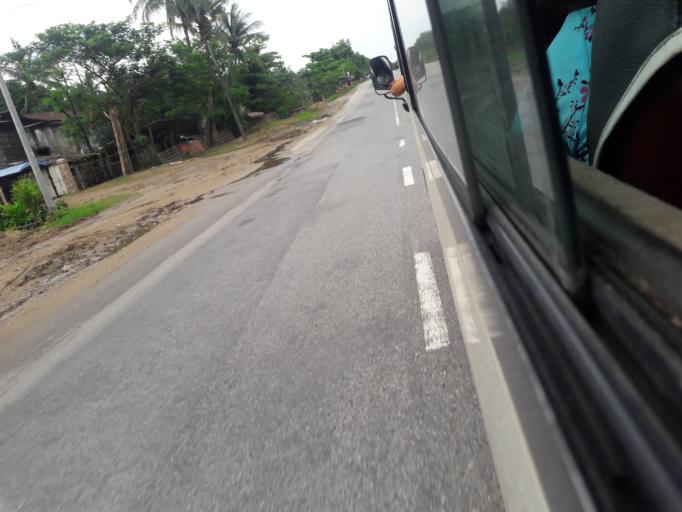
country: MM
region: Bago
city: Nyaunglebin
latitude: 17.8328
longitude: 96.6782
